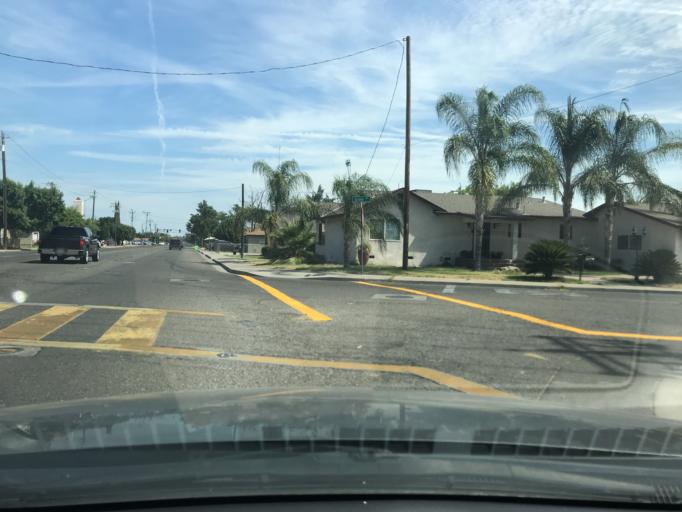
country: US
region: California
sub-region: Merced County
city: Atwater
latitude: 37.3533
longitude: -120.6137
